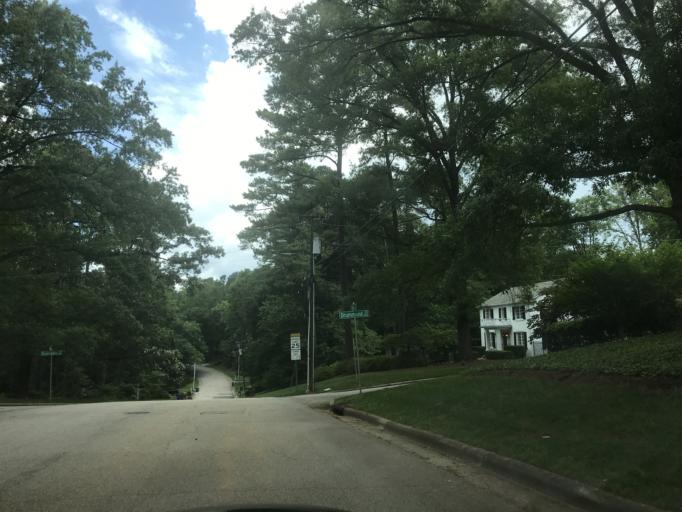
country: US
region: North Carolina
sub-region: Wake County
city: West Raleigh
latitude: 35.8275
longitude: -78.6443
